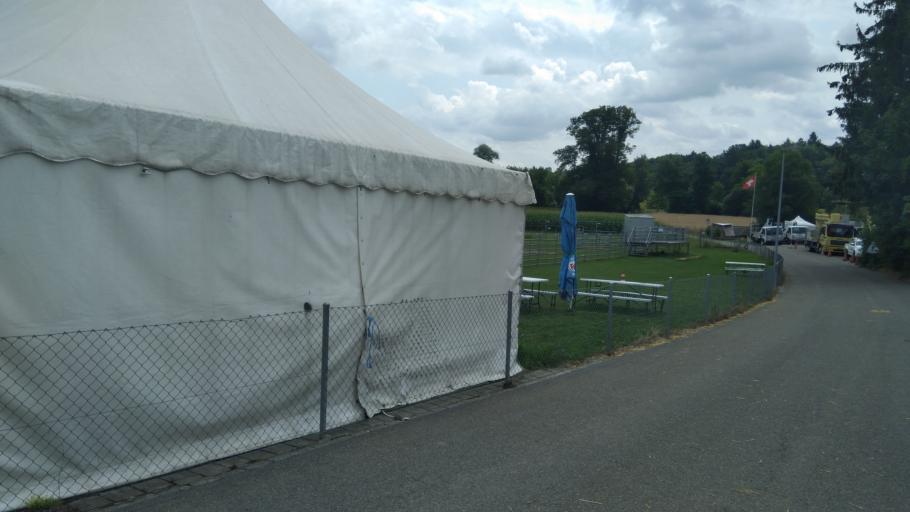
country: CH
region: Zurich
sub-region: Bezirk Dielsdorf
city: Oberglatt / Oberglatt (Dorfkern)
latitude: 47.4761
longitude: 8.5287
